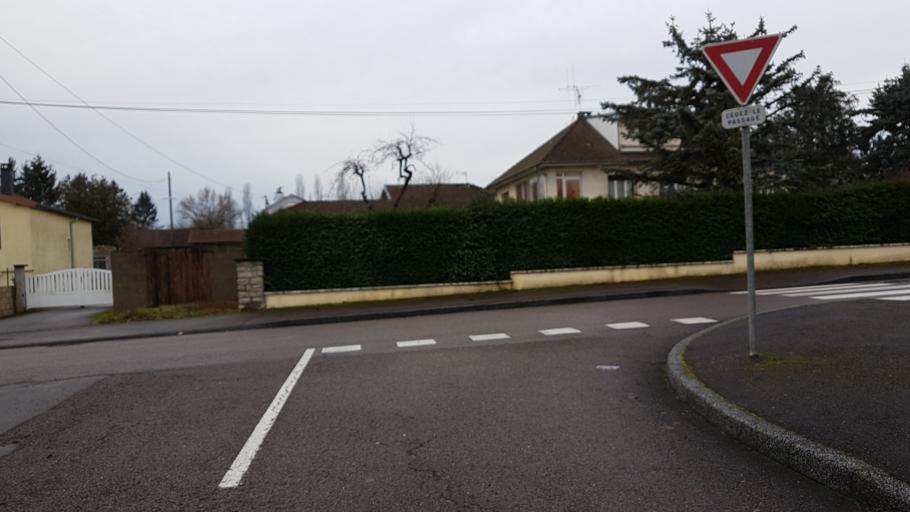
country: FR
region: Franche-Comte
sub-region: Departement de la Haute-Saone
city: Luxeuil-les-Bains
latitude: 47.8122
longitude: 6.3670
